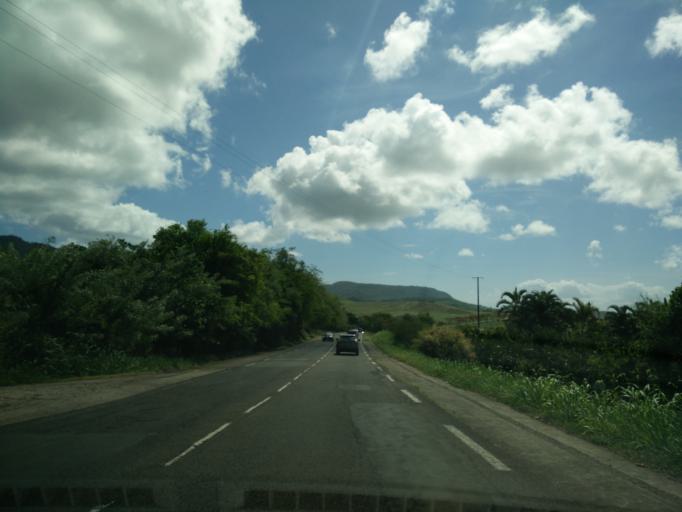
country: MQ
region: Martinique
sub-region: Martinique
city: Les Trois-Ilets
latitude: 14.5284
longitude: -61.0032
